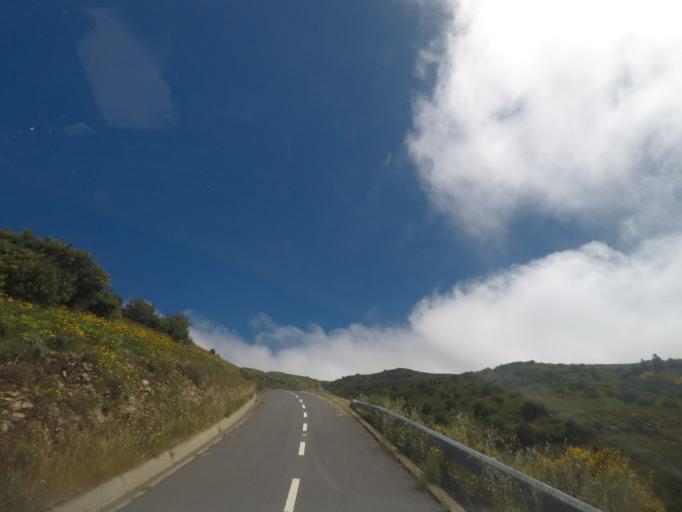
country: PT
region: Madeira
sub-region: Camara de Lobos
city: Curral das Freiras
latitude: 32.7100
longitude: -16.9396
